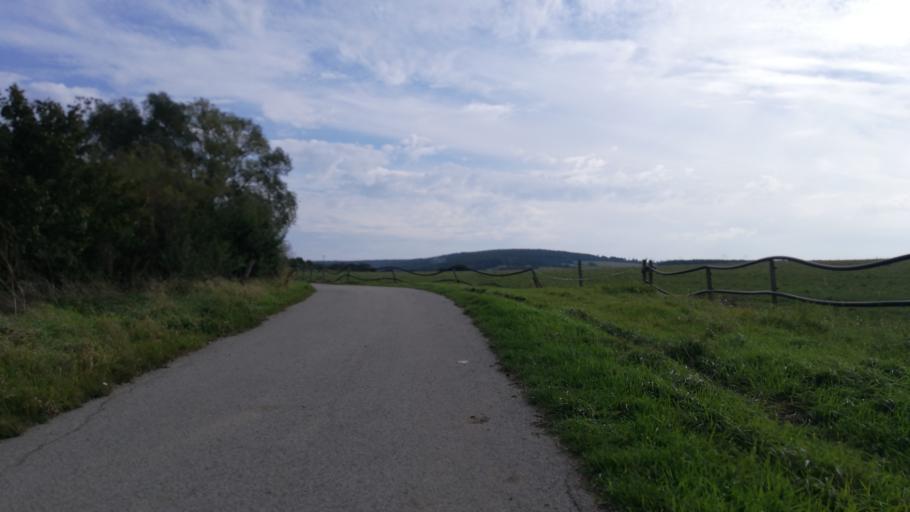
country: CZ
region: South Moravian
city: Sudomerice
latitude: 48.8411
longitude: 17.2829
